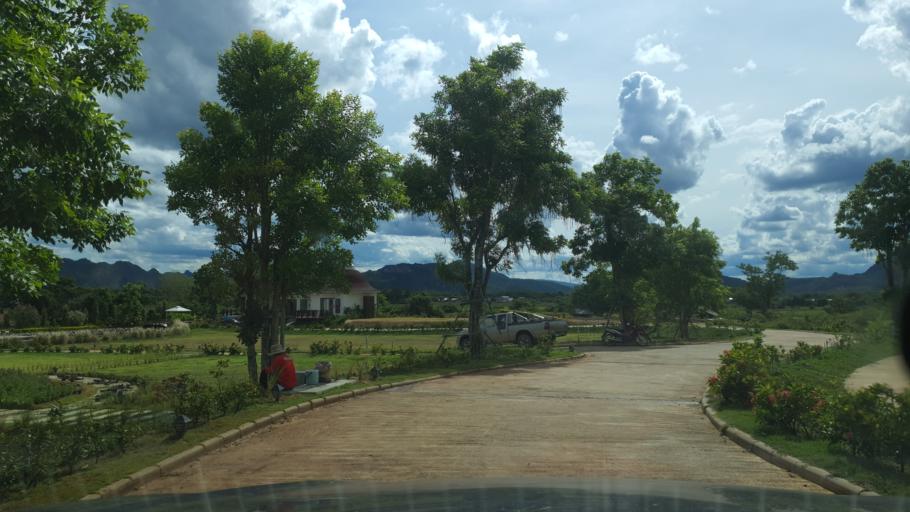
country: TH
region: Sukhothai
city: Thung Saliam
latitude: 17.3268
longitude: 99.5439
